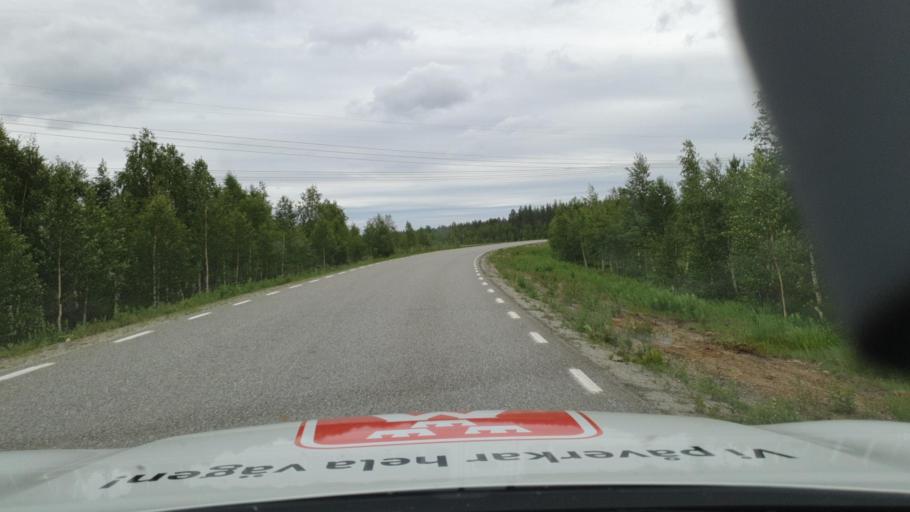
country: SE
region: Vaesterbotten
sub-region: Lycksele Kommun
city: Lycksele
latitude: 64.1644
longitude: 18.3579
